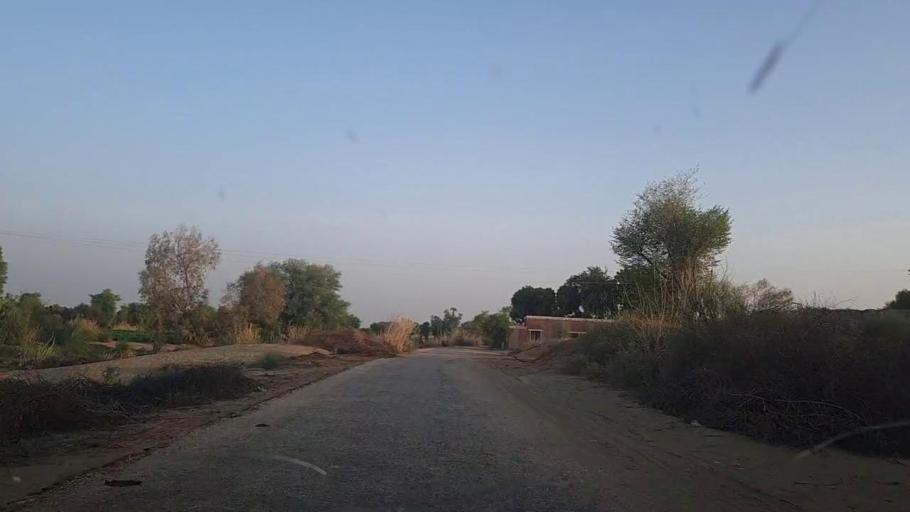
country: PK
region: Sindh
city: Khanpur
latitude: 27.6245
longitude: 69.4445
